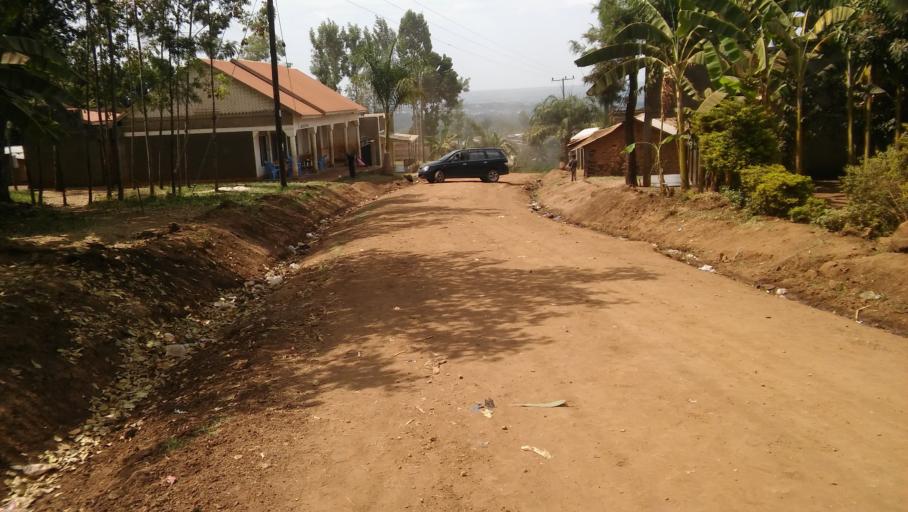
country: UG
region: Eastern Region
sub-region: Mbale District
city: Mbale
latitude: 1.0585
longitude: 34.2110
